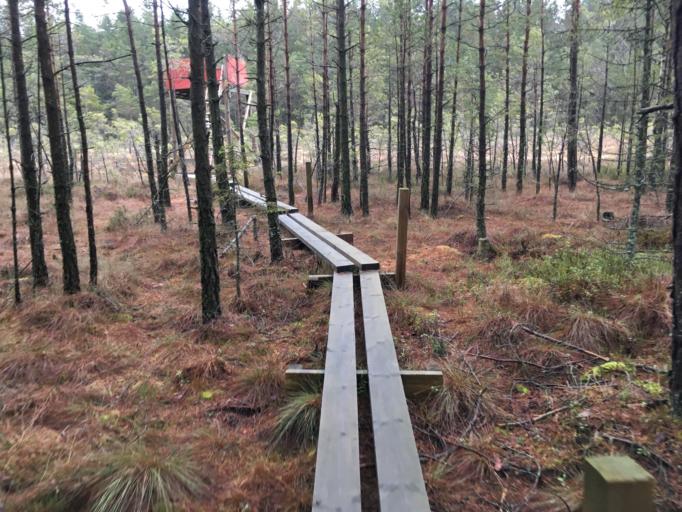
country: SE
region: Vaestra Goetaland
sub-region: Alingsas Kommun
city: Alingsas
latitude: 57.9014
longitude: 12.6259
